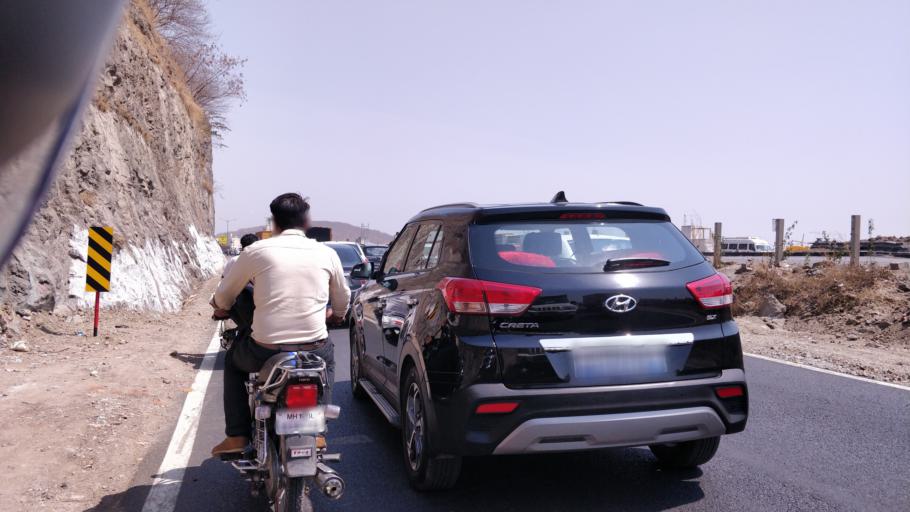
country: IN
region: Maharashtra
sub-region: Pune Division
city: Shivaji Nagar
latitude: 18.5360
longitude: 73.7806
